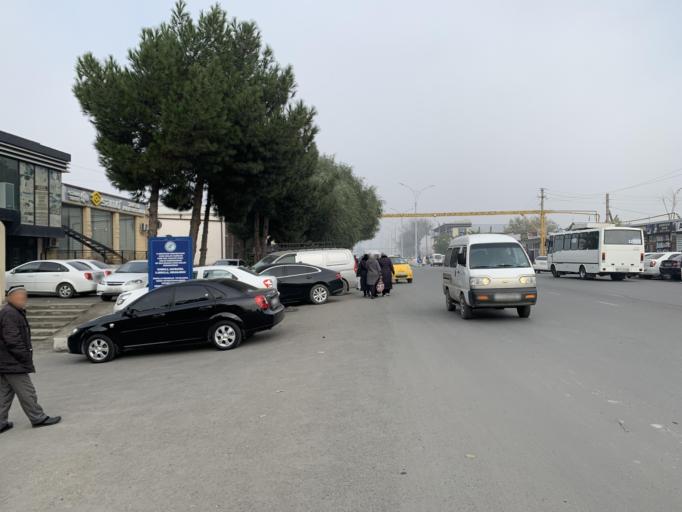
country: UZ
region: Fergana
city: Qo`qon
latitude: 40.5488
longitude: 70.9587
